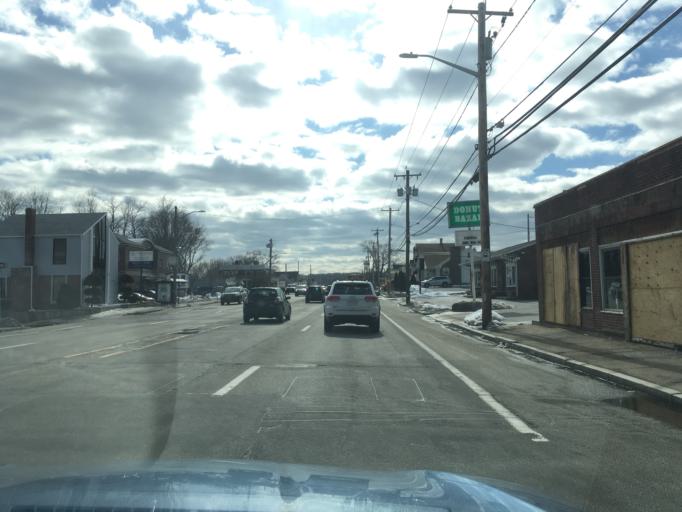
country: US
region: Rhode Island
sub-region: Providence County
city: Cranston
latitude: 41.7782
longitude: -71.4455
